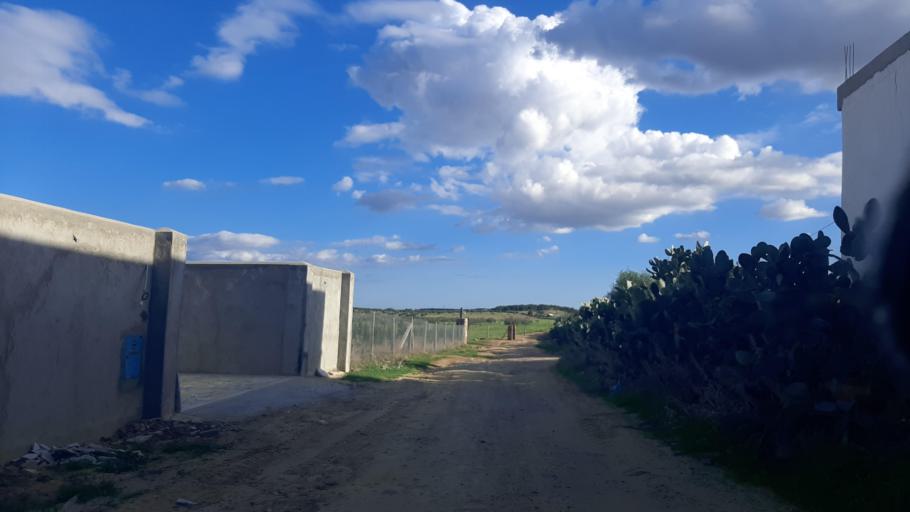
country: TN
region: Nabul
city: Bu `Urqub
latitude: 36.4651
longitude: 10.4825
